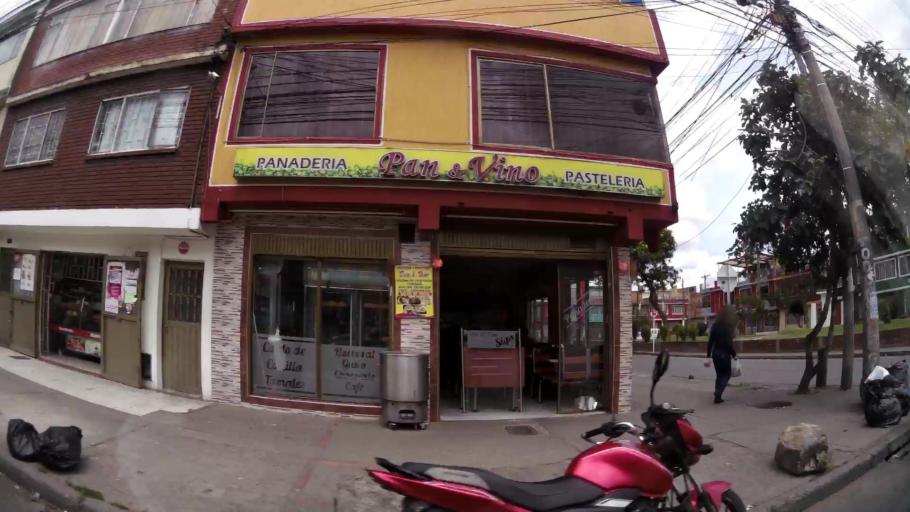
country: CO
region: Cundinamarca
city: Funza
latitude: 4.7086
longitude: -74.1175
